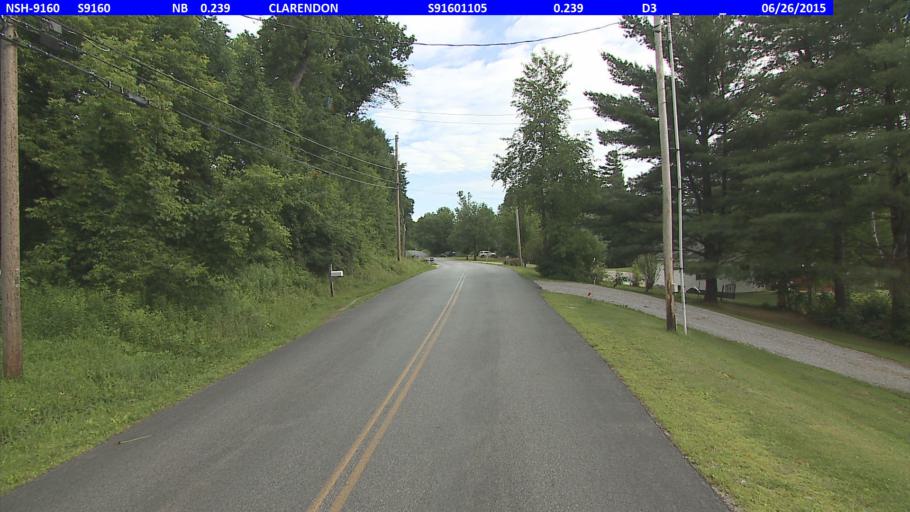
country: US
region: Vermont
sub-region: Rutland County
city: Rutland
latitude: 43.5311
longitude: -72.9451
